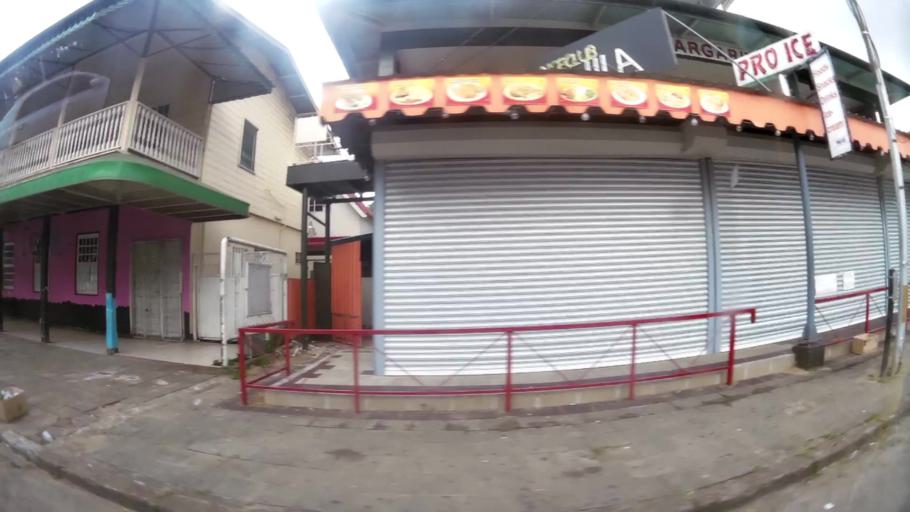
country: SR
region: Paramaribo
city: Paramaribo
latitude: 5.8284
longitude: -55.1484
